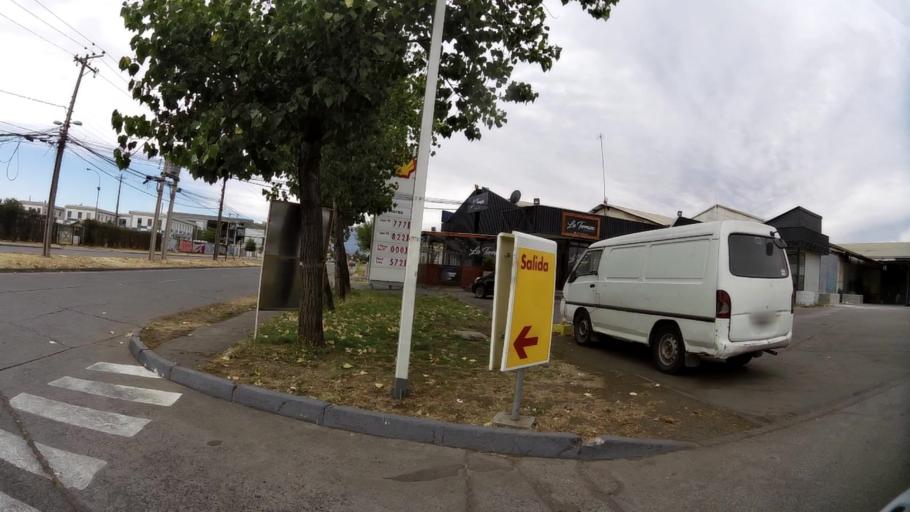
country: CL
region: O'Higgins
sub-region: Provincia de Cachapoal
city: Rancagua
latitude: -34.1380
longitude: -70.7414
